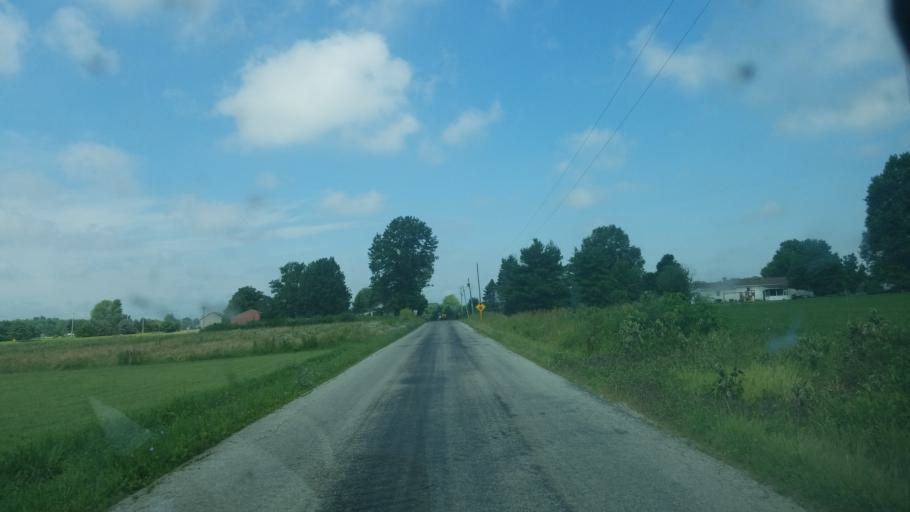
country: US
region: Ohio
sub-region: Licking County
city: Johnstown
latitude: 40.2080
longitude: -82.7532
